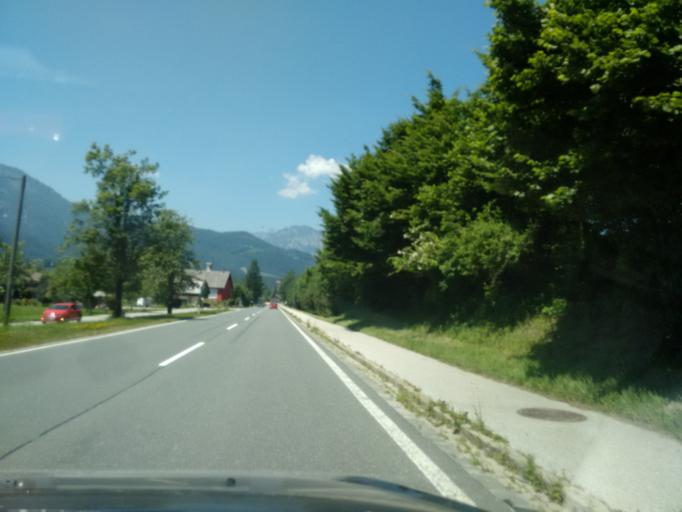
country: AT
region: Upper Austria
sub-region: Politischer Bezirk Gmunden
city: Bad Goisern
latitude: 47.6284
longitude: 13.6373
